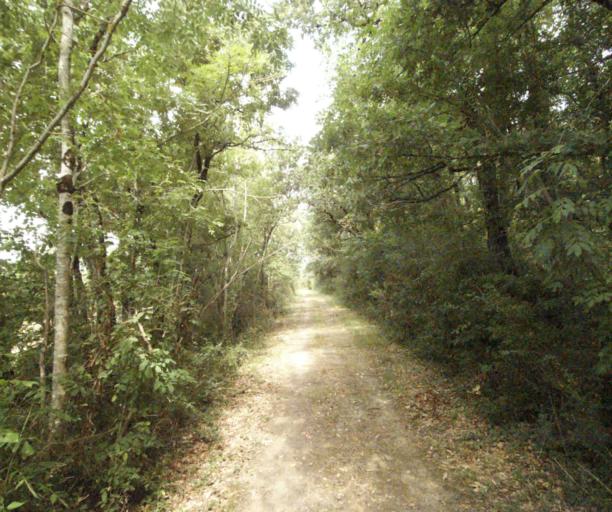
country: FR
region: Midi-Pyrenees
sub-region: Departement de la Haute-Garonne
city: Saint-Felix-Lauragais
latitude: 43.4242
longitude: 1.9296
